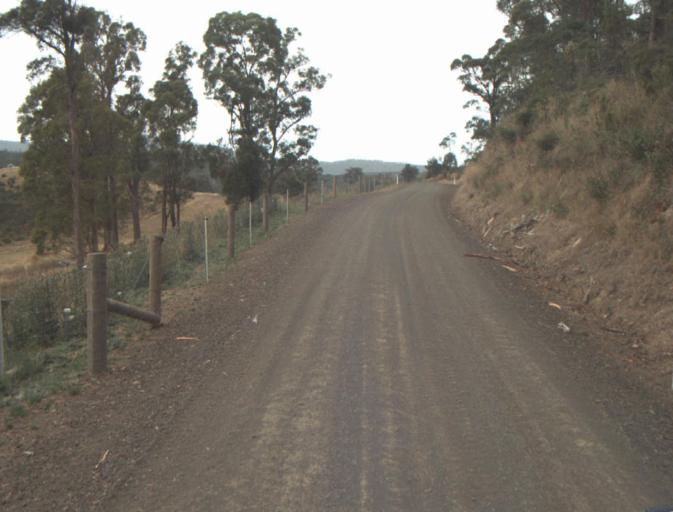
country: AU
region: Tasmania
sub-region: Northern Midlands
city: Evandale
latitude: -41.4687
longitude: 147.5354
